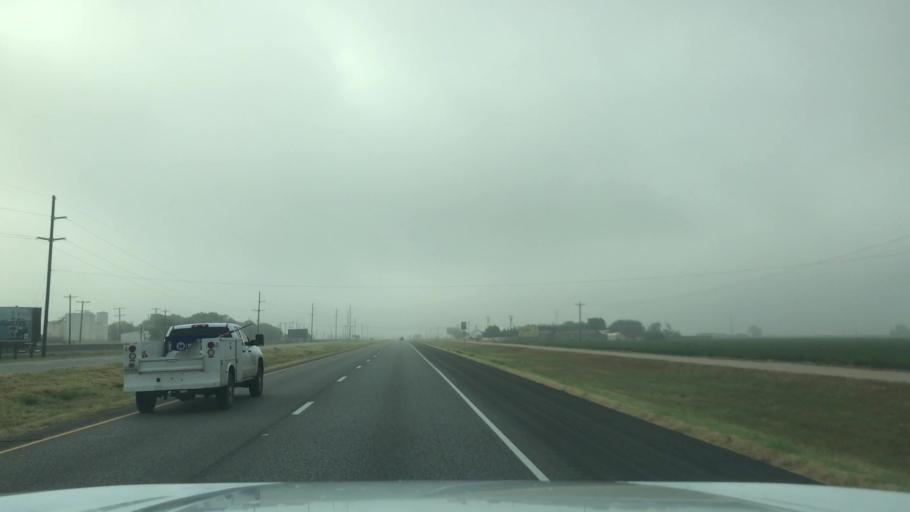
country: US
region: Texas
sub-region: Lubbock County
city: Ransom Canyon
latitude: 33.4853
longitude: -101.7157
